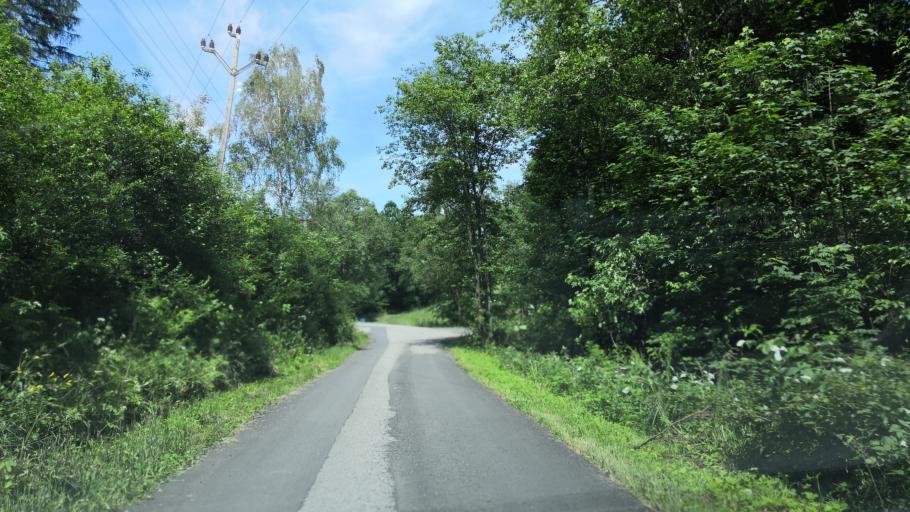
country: CZ
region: Zlin
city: Valasska Bystrice
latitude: 49.4213
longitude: 18.0980
